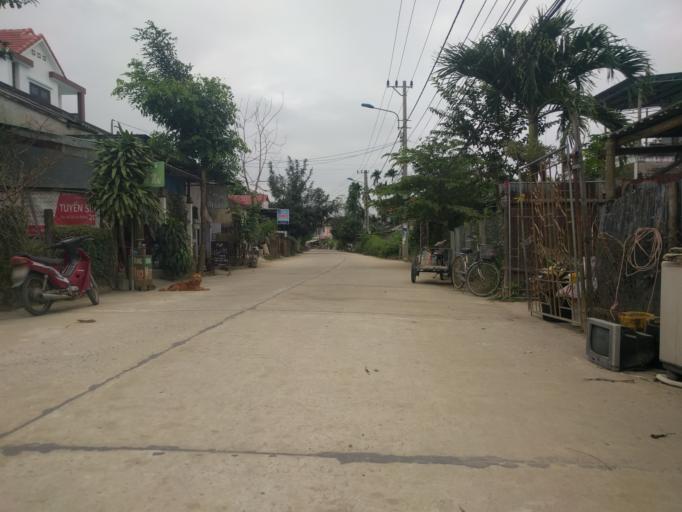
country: VN
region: Quang Nam
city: Hoi An
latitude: 15.8696
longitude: 108.3502
